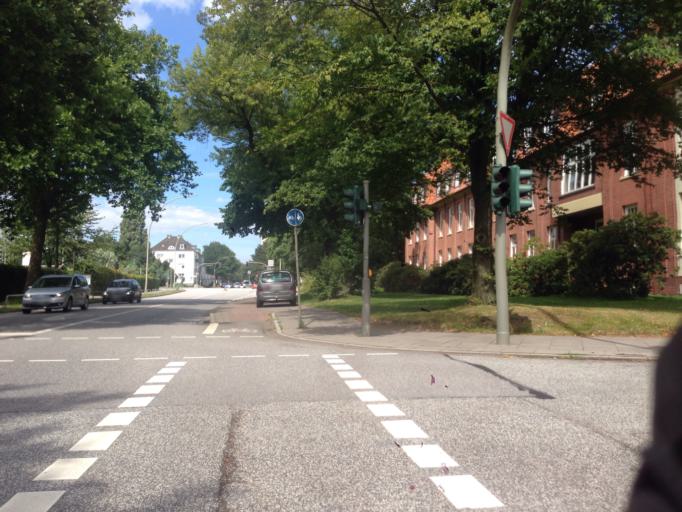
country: DE
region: Hamburg
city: Barmbek-Nord
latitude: 53.6062
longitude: 10.0343
